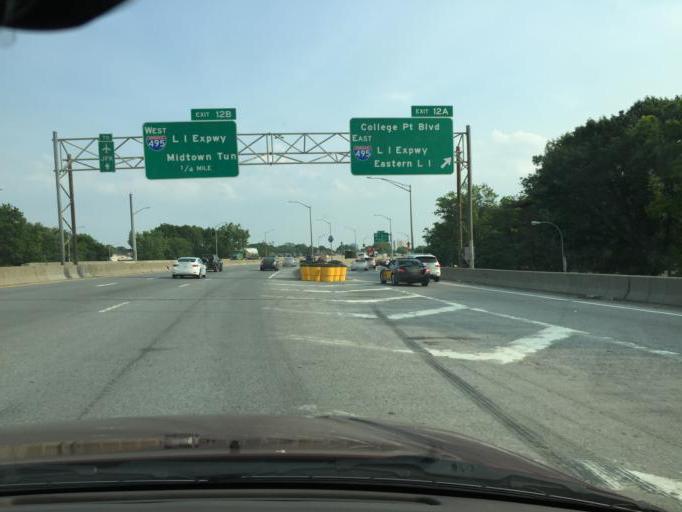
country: US
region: New York
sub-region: Queens County
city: Jamaica
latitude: 40.7493
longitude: -73.8349
